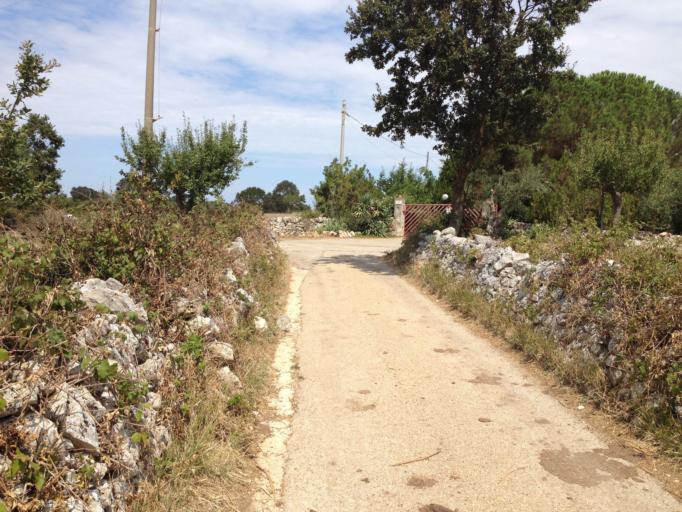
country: IT
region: Apulia
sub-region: Provincia di Bari
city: Gioia del Colle
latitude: 40.8254
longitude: 16.9799
